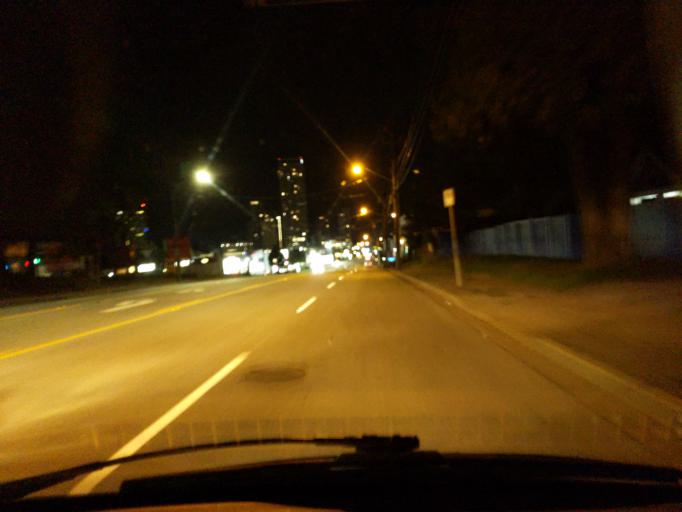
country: CA
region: British Columbia
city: New Westminster
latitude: 49.1916
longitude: -122.8358
